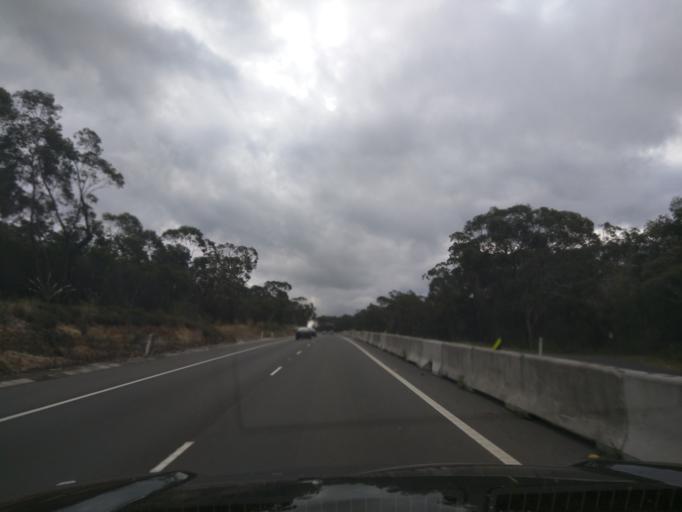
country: AU
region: New South Wales
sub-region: Wollongong
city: Mount Keira
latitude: -34.3659
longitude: 150.8246
